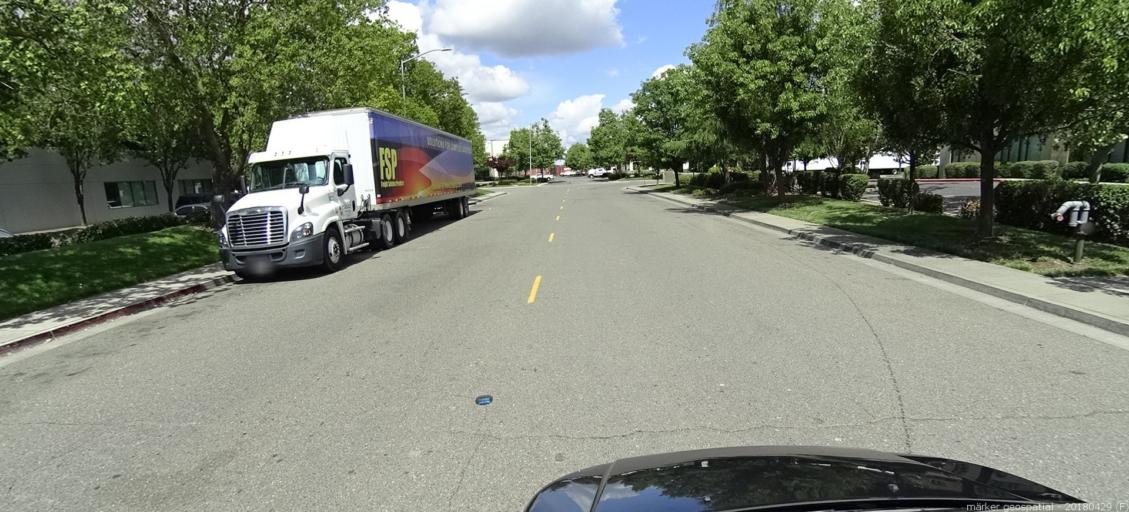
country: US
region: California
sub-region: Yolo County
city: West Sacramento
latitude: 38.5899
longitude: -121.5640
